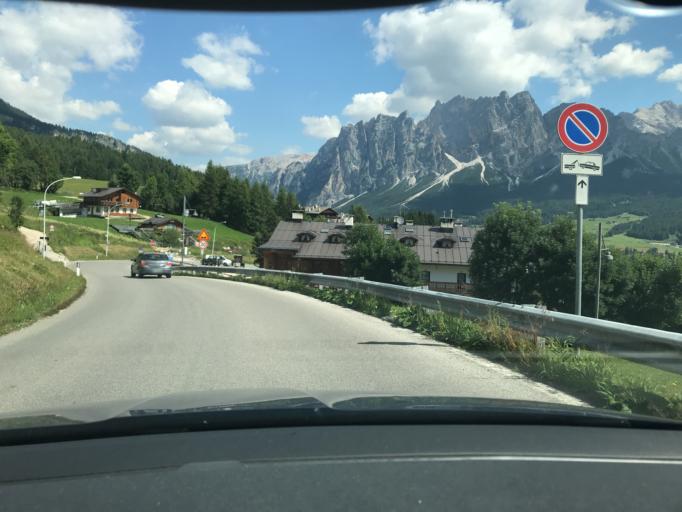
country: IT
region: Veneto
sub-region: Provincia di Belluno
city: Cortina d'Ampezzo
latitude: 46.5316
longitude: 12.1213
